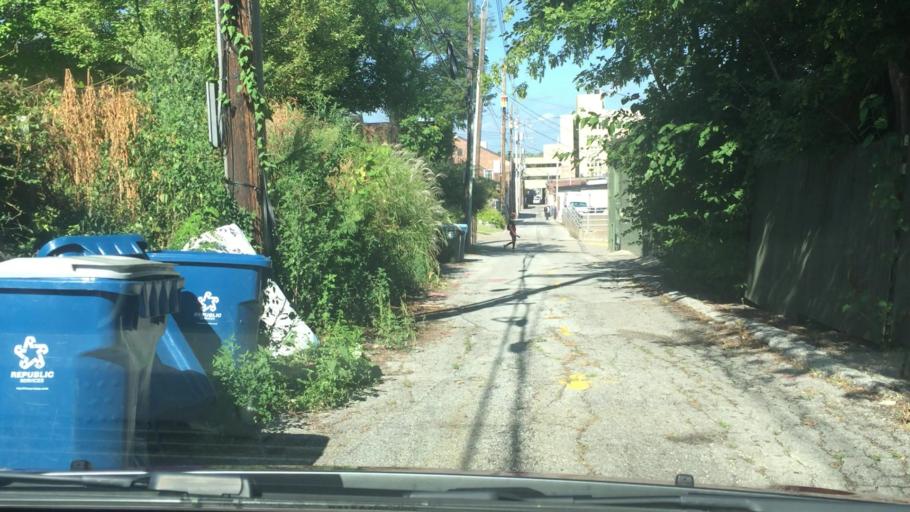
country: US
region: Iowa
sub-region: Muscatine County
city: Muscatine
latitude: 41.4202
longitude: -91.0488
